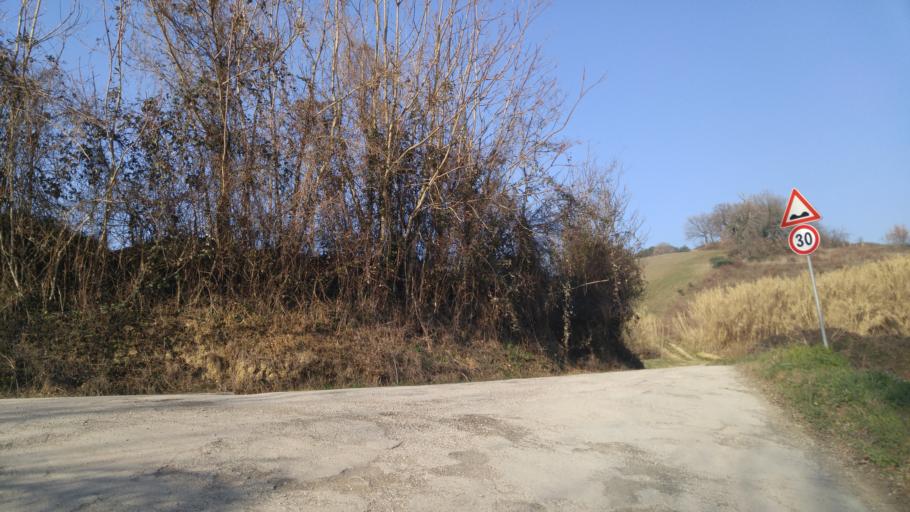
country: IT
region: The Marches
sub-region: Provincia di Pesaro e Urbino
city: Cuccurano
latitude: 43.8167
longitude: 12.9347
